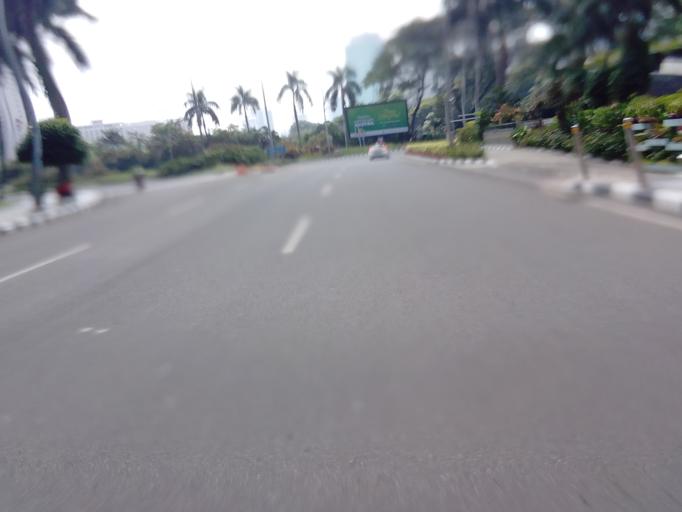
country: ID
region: Jakarta Raya
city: Jakarta
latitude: -6.2242
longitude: 106.8087
